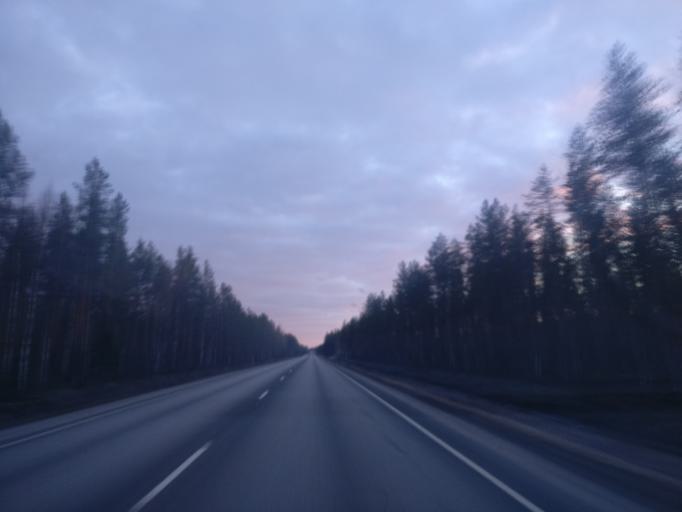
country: FI
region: Northern Ostrobothnia
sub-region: Nivala-Haapajaervi
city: Kaersaemaeki
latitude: 64.0948
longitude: 25.8011
